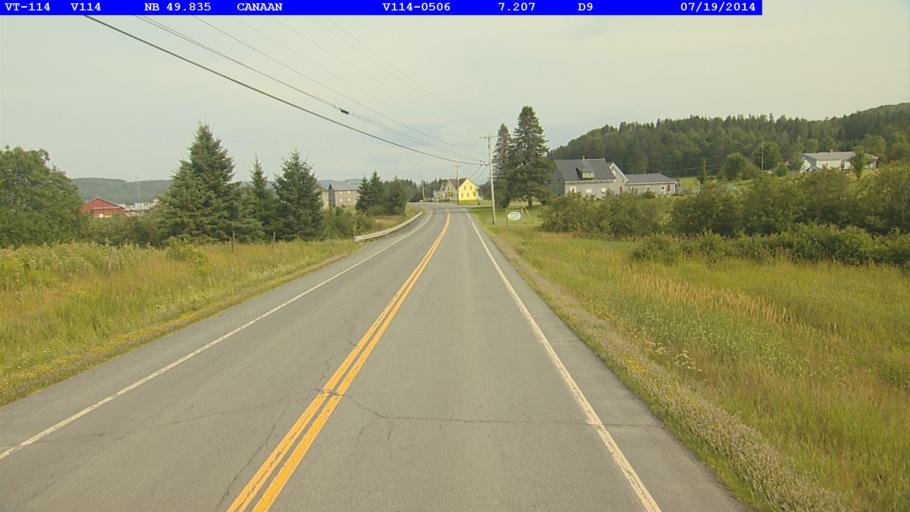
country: US
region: New Hampshire
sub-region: Coos County
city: Colebrook
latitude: 45.0049
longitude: -71.5539
